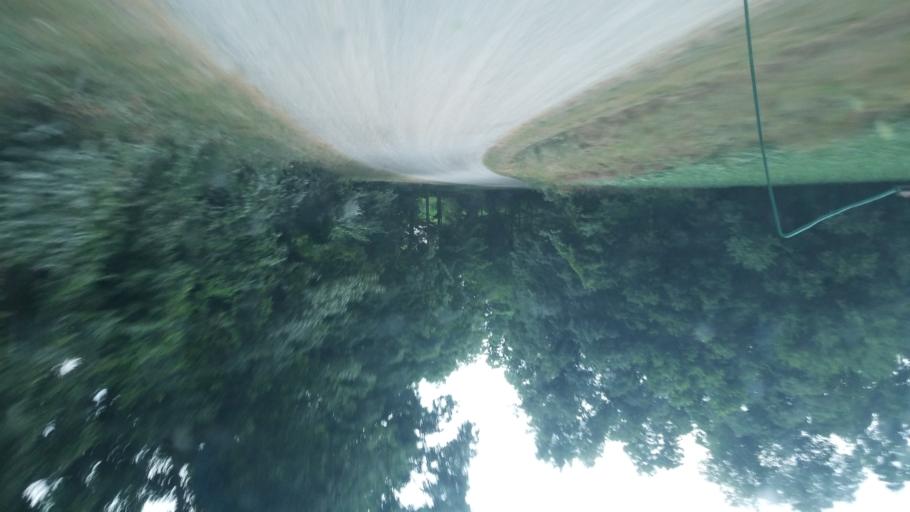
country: US
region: Ohio
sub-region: Defiance County
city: Hicksville
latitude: 41.3390
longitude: -84.8406
